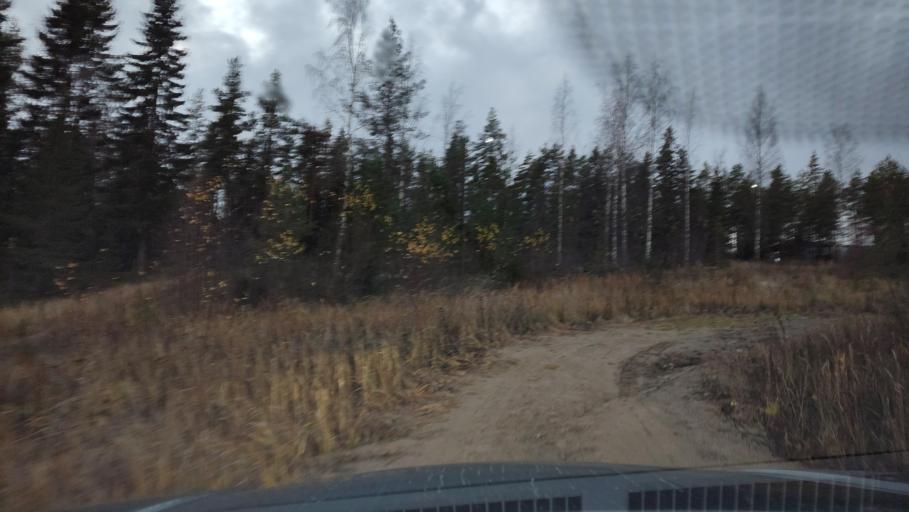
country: FI
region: Southern Ostrobothnia
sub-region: Suupohja
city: Karijoki
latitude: 62.2809
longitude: 21.6297
